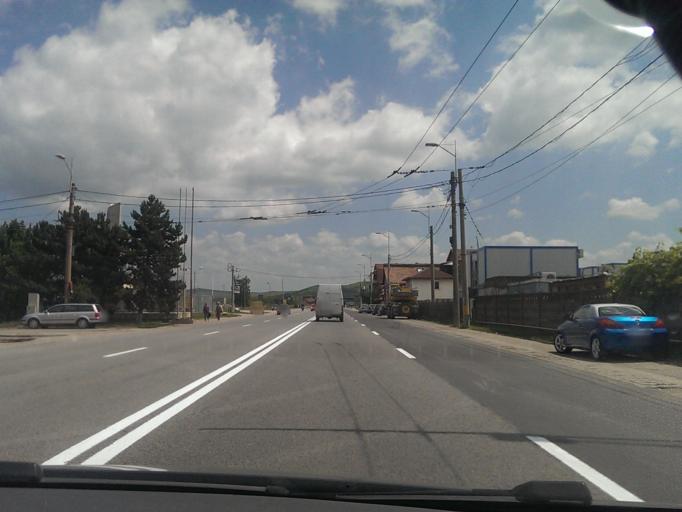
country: RO
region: Cluj
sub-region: Comuna Apahida
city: Sannicoara
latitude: 46.7819
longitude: 23.6978
